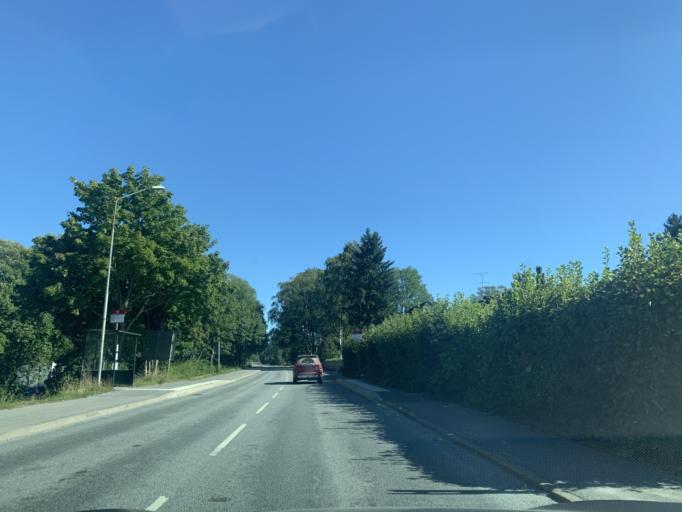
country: SE
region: Stockholm
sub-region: Ekero Kommun
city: Ekeroe
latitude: 59.2890
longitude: 17.8124
